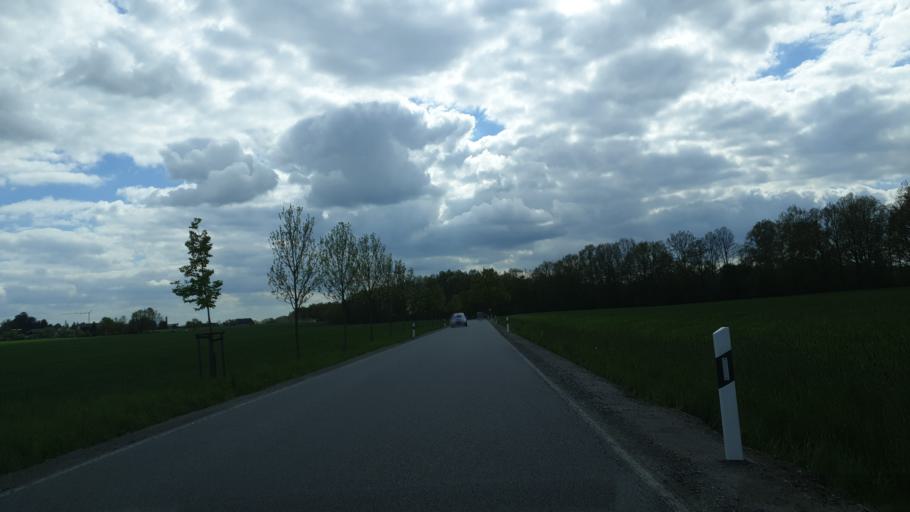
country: DE
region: Saxony
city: Niederdorf
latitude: 50.7686
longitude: 12.7794
